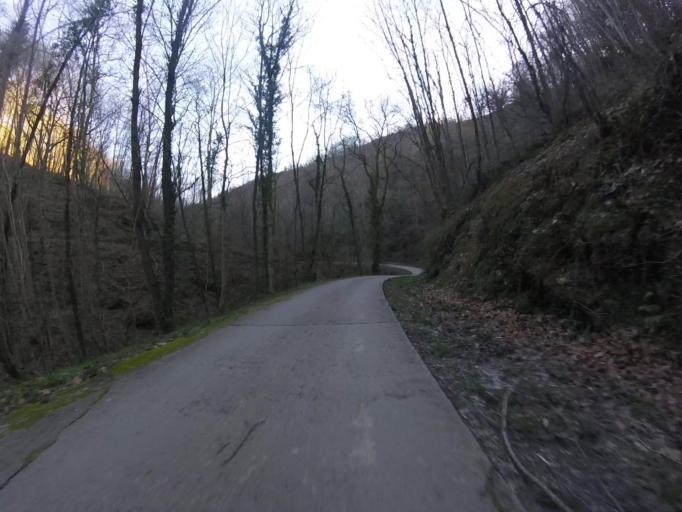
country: ES
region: Basque Country
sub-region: Provincia de Guipuzcoa
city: Errenteria
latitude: 43.2738
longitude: -1.8660
